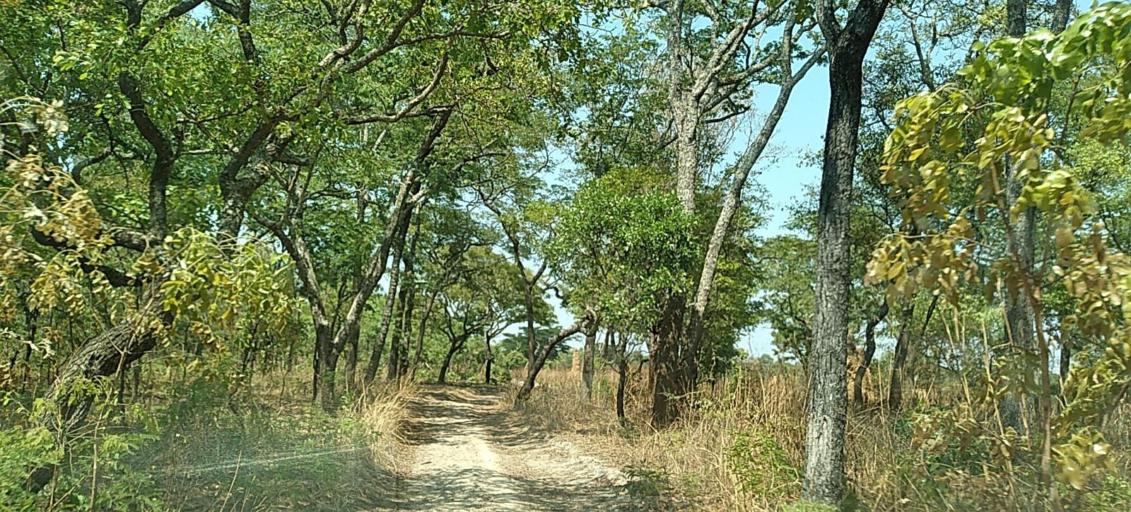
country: ZM
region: Copperbelt
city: Mpongwe
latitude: -13.7918
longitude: 28.0911
